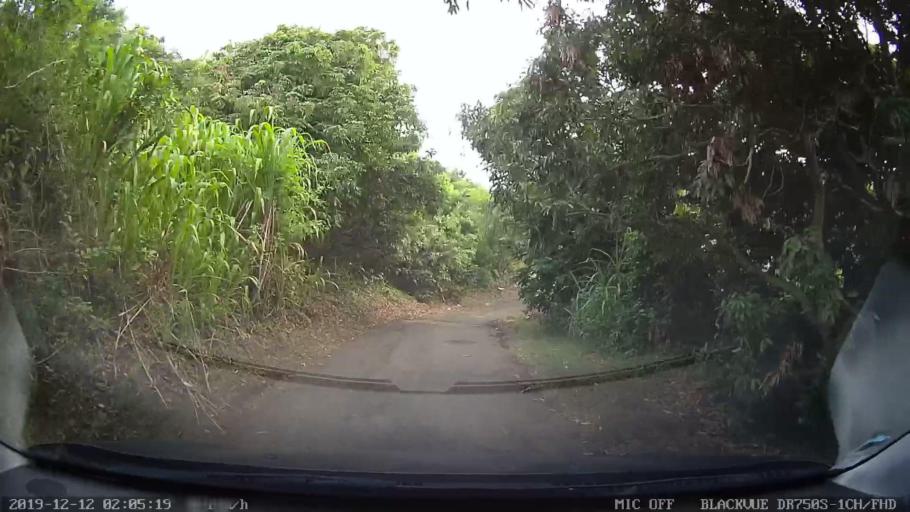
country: RE
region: Reunion
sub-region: Reunion
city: Sainte-Marie
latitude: -20.9331
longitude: 55.5287
